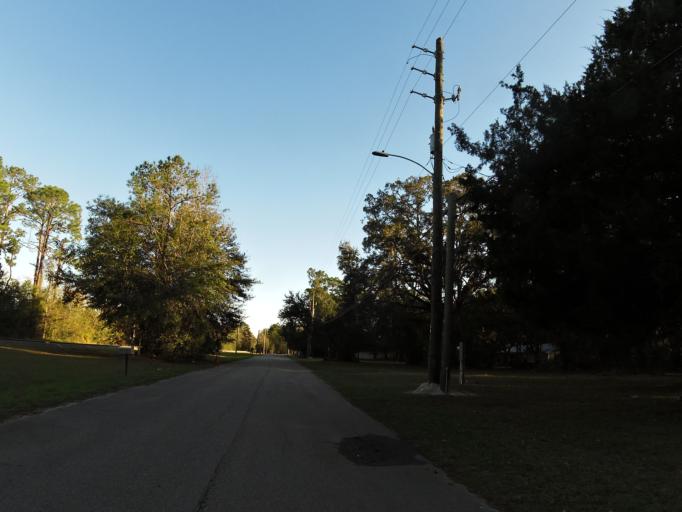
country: US
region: Florida
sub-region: Saint Johns County
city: Fruit Cove
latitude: 30.2022
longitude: -81.5763
